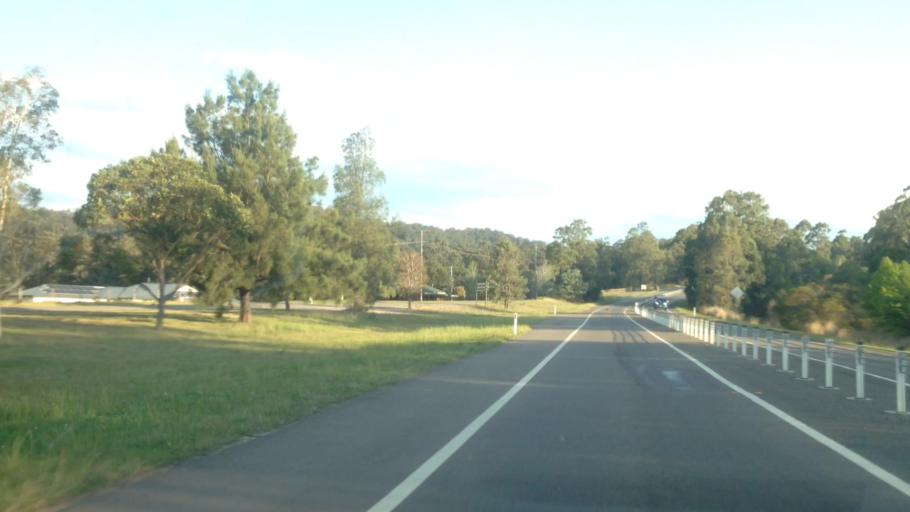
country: AU
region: New South Wales
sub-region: Lake Macquarie Shire
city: Holmesville
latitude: -32.9531
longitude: 151.4798
